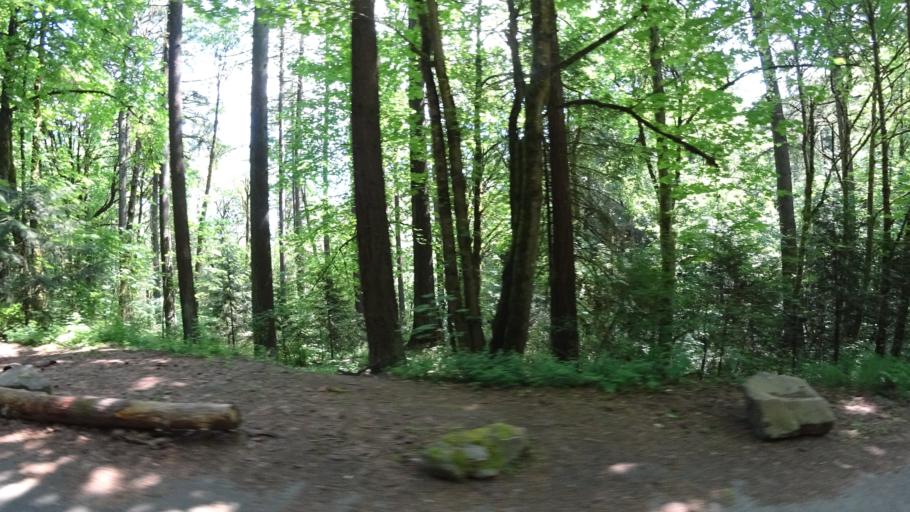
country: US
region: Oregon
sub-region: Multnomah County
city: Portland
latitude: 45.5198
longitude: -122.7186
